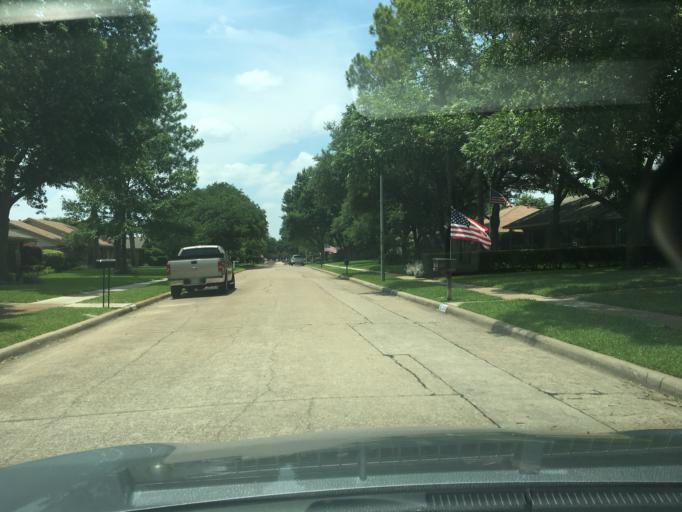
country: US
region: Texas
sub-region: Dallas County
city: Richardson
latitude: 32.9557
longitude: -96.6867
